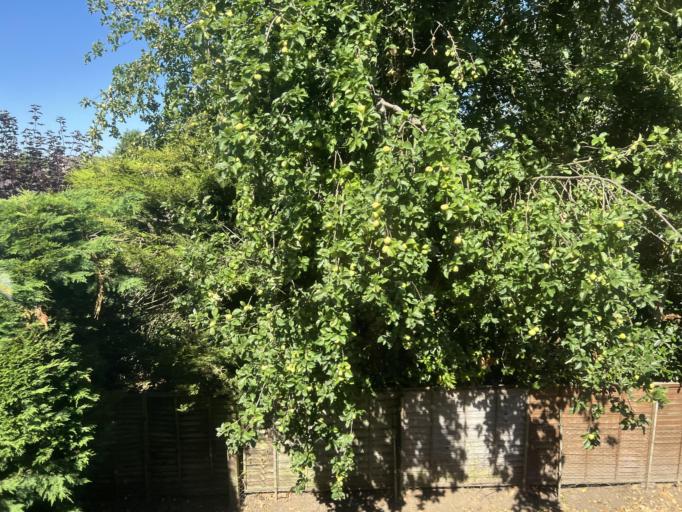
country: GB
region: England
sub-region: Lincolnshire
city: Boston
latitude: 52.9893
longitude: -0.0321
